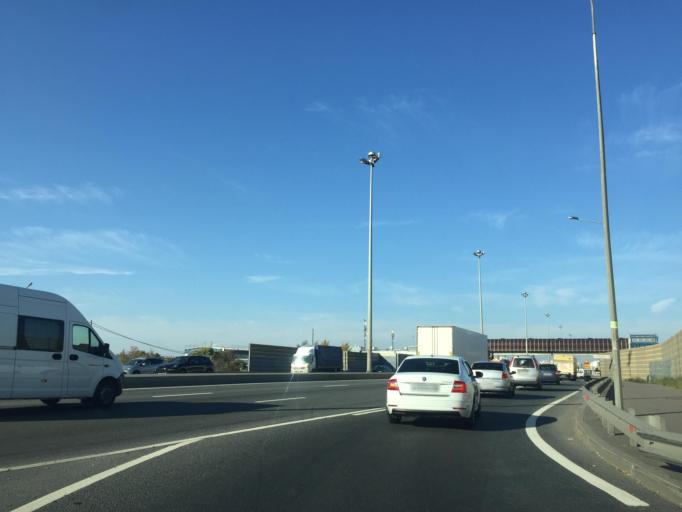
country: RU
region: St.-Petersburg
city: Petro-Slavyanka
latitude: 59.7462
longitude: 30.5017
